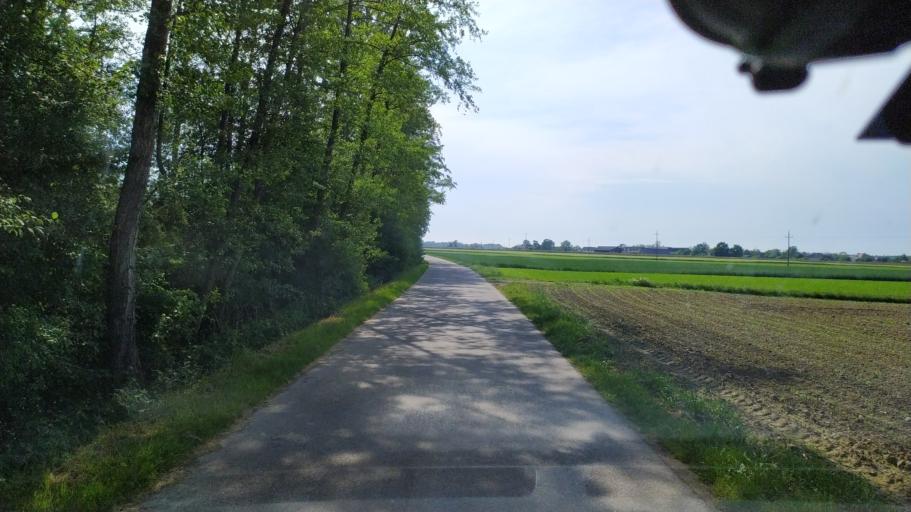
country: AT
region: Lower Austria
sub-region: Politischer Bezirk Amstetten
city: Zeillern
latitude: 48.1936
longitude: 14.7341
